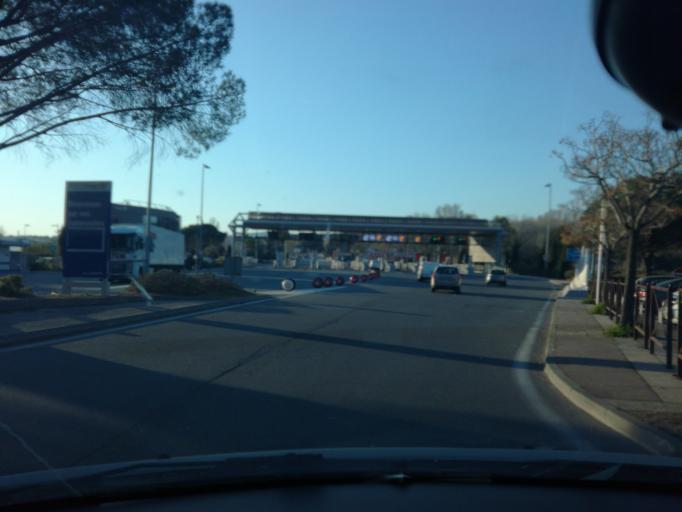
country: FR
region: Provence-Alpes-Cote d'Azur
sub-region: Departement du Var
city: Frejus
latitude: 43.4714
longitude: 6.7442
